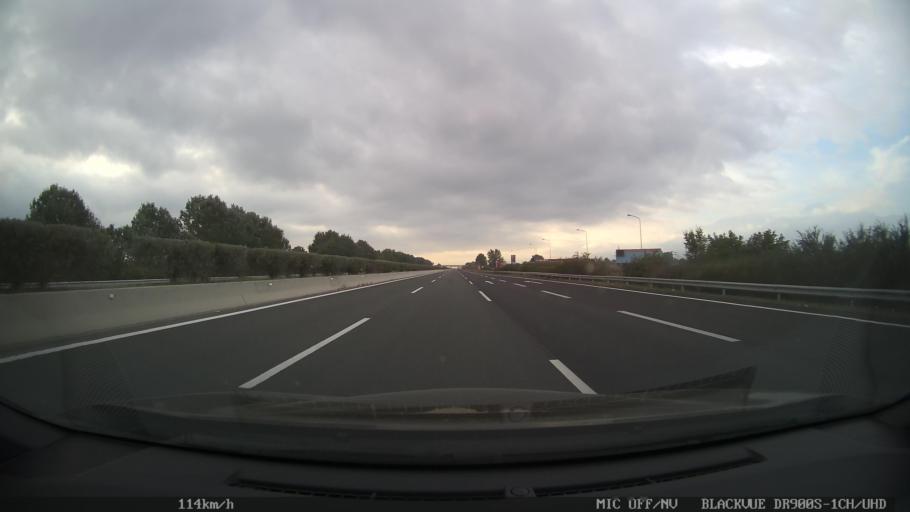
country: GR
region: Central Macedonia
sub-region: Nomos Pierias
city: Nea Efesos
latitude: 40.2333
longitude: 22.5379
